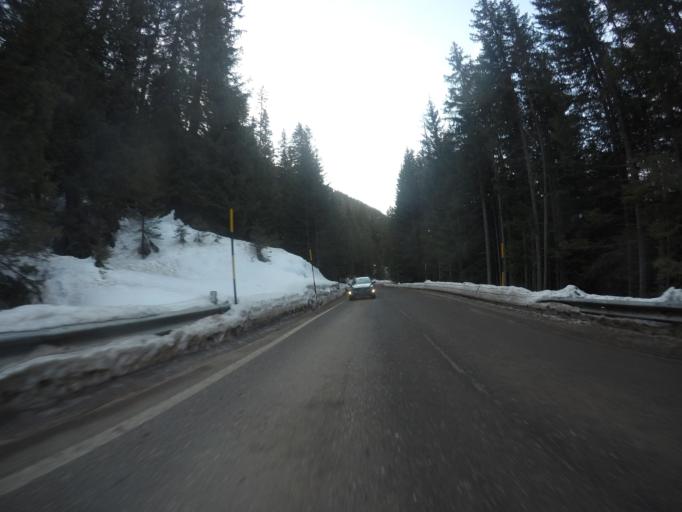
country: IT
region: Trentino-Alto Adige
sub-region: Provincia di Trento
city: Canazei
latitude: 46.4897
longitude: 11.7836
